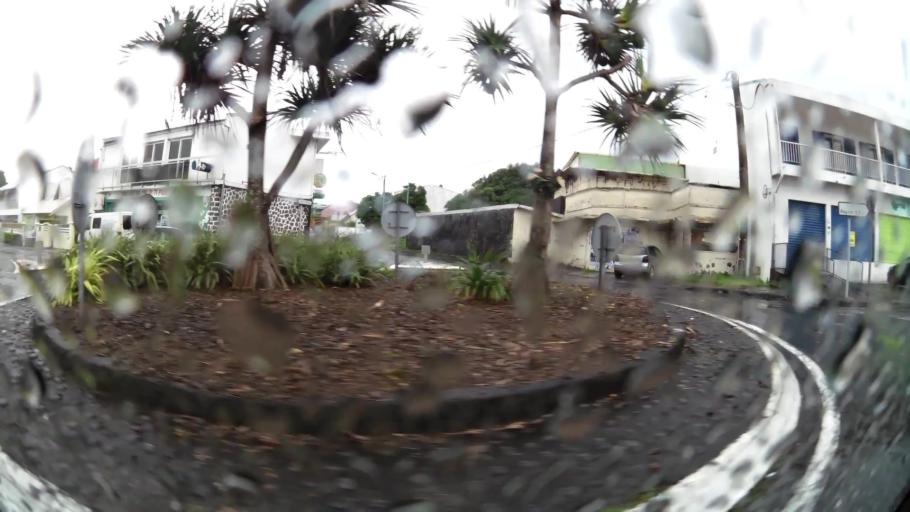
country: RE
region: Reunion
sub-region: Reunion
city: Saint-Benoit
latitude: -21.0395
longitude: 55.7220
